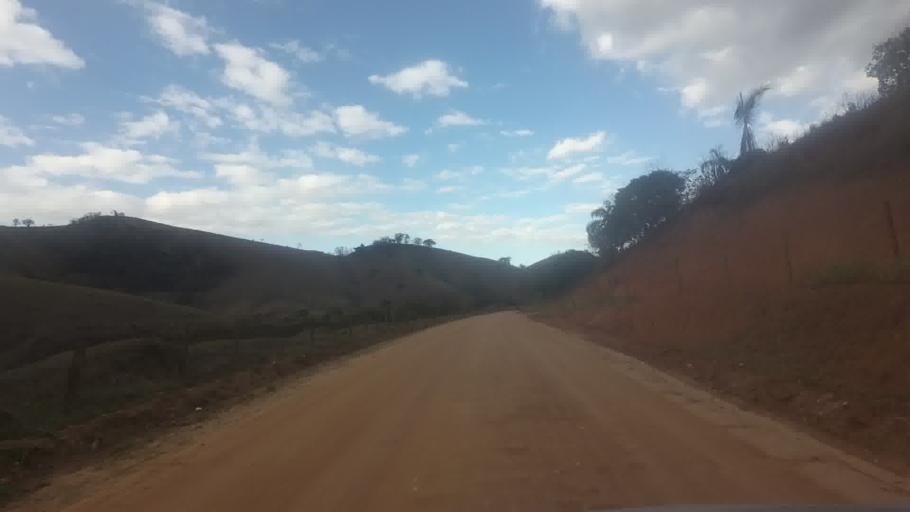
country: BR
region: Espirito Santo
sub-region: Mimoso Do Sul
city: Mimoso do Sul
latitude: -20.9463
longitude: -41.3746
